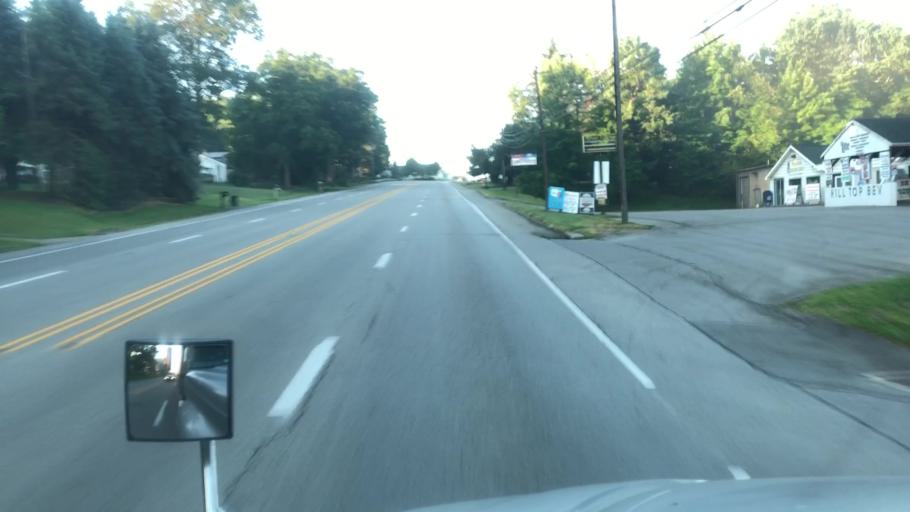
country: US
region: Pennsylvania
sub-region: Venango County
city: Franklin
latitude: 41.3824
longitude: -79.8503
